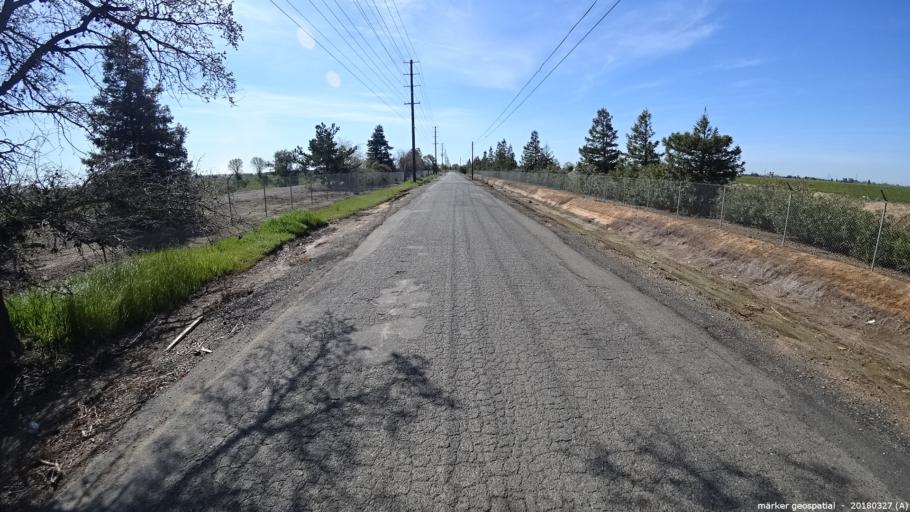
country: US
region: California
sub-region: Sacramento County
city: Rosemont
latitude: 38.5241
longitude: -121.3442
